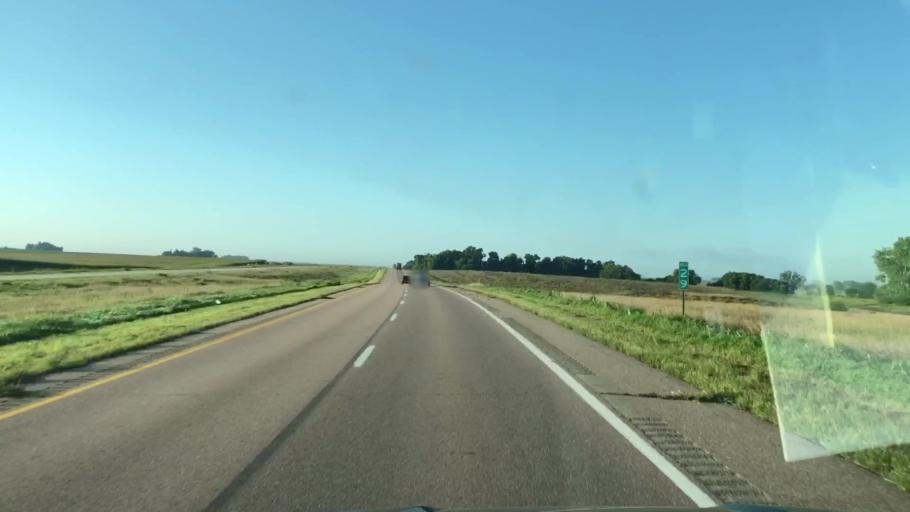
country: US
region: Iowa
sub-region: O'Brien County
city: Sheldon
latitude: 43.1405
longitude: -95.8809
